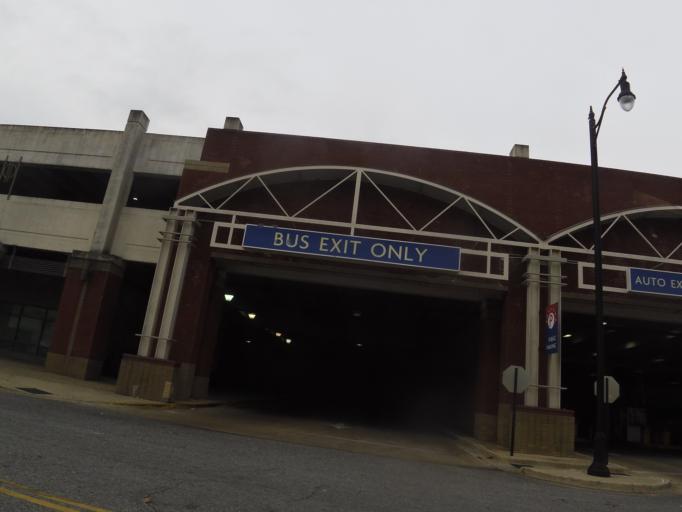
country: US
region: Alabama
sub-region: Montgomery County
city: Montgomery
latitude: 32.3796
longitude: -86.3148
